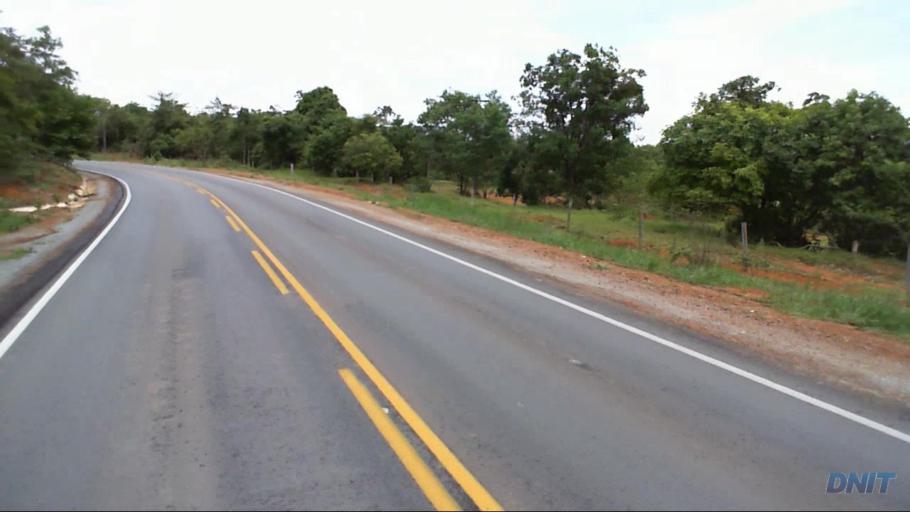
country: BR
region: Goias
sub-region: Padre Bernardo
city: Padre Bernardo
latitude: -15.5067
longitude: -48.1977
